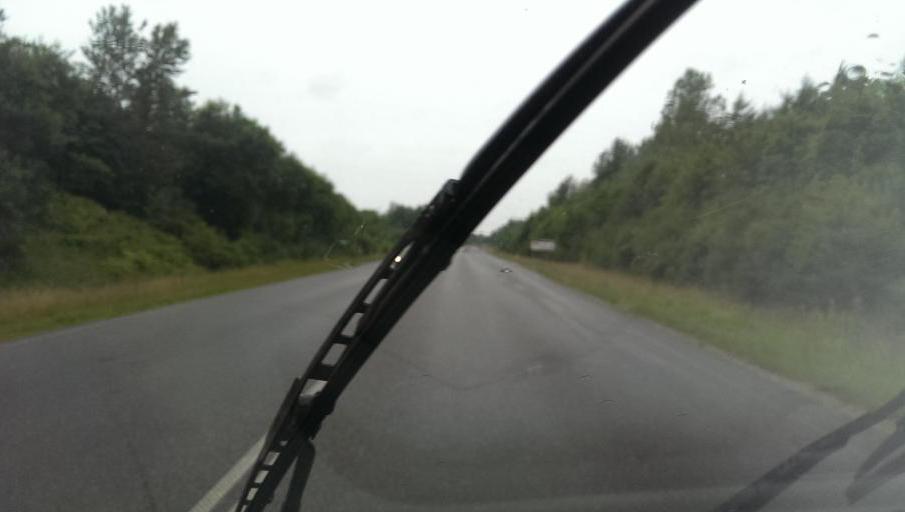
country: DK
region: South Denmark
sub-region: Esbjerg Kommune
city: Esbjerg
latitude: 55.5189
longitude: 8.4640
